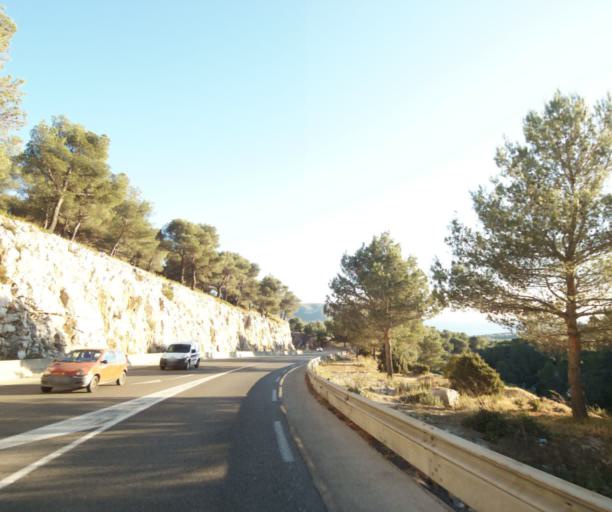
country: FR
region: Provence-Alpes-Cote d'Azur
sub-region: Departement des Bouches-du-Rhone
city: Carnoux-en-Provence
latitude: 43.2402
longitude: 5.5436
